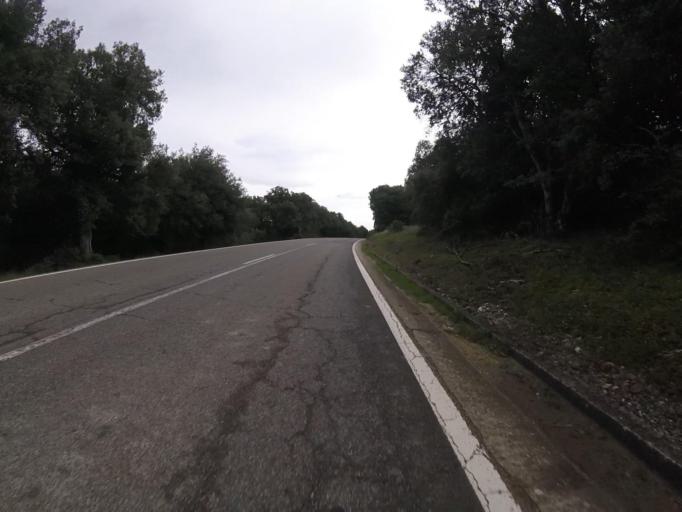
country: ES
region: Navarre
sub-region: Provincia de Navarra
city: Lezaun
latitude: 42.7510
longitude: -2.0151
